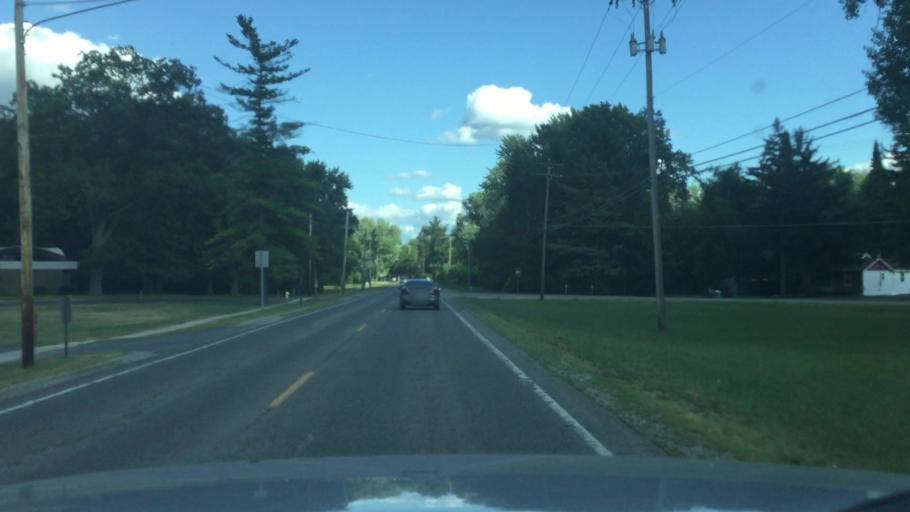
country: US
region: Michigan
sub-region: Saginaw County
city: Bridgeport
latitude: 43.3655
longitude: -83.8948
